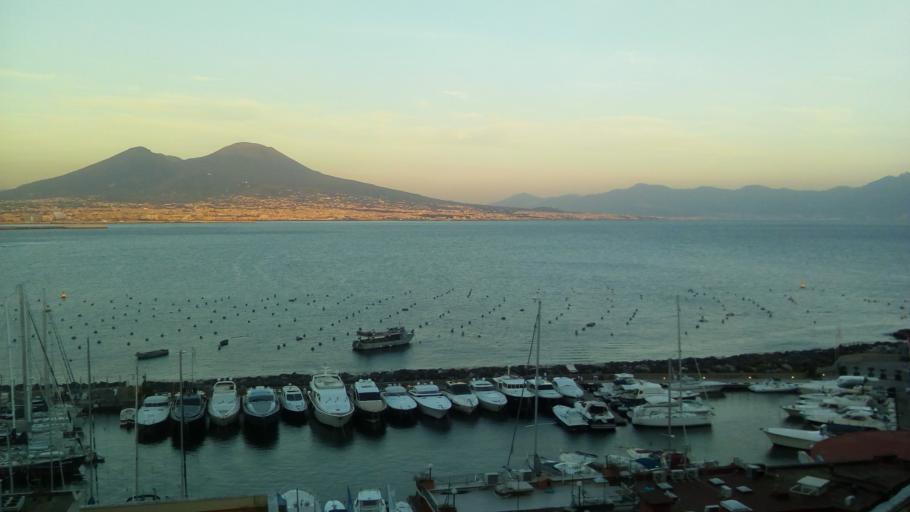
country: IT
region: Campania
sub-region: Provincia di Napoli
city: Napoli
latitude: 40.8281
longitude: 14.2482
